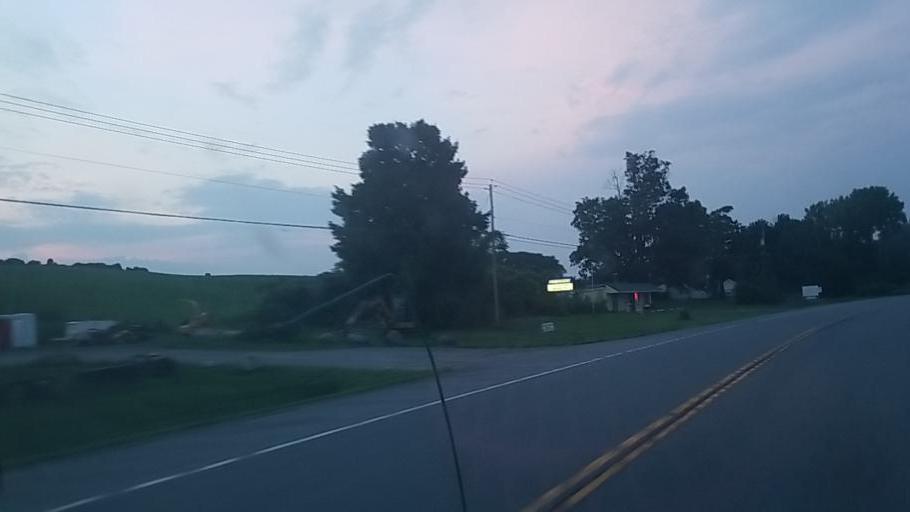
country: US
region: New York
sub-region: Montgomery County
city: Fonda
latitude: 42.9807
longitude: -74.3905
